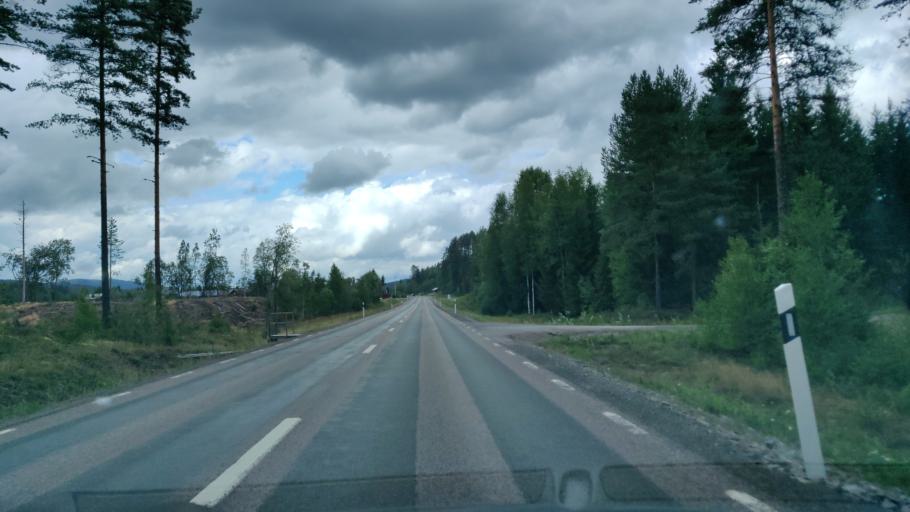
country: SE
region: Vaermland
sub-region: Torsby Kommun
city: Torsby
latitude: 60.5363
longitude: 13.1218
